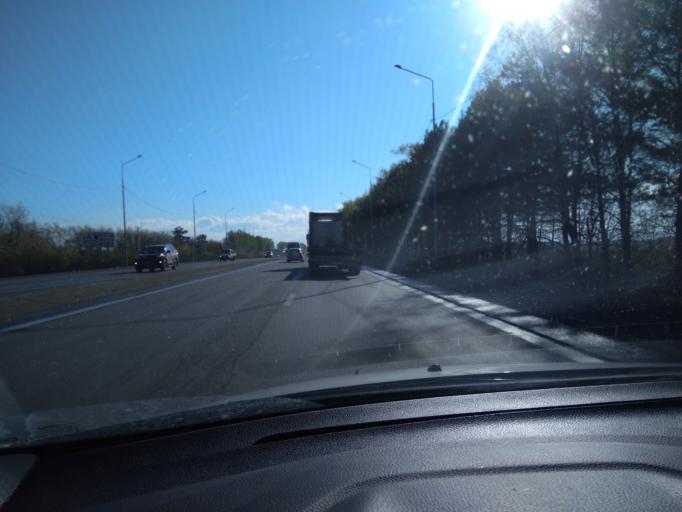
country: RU
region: Tjumen
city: Moskovskiy
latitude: 57.1223
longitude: 65.4532
